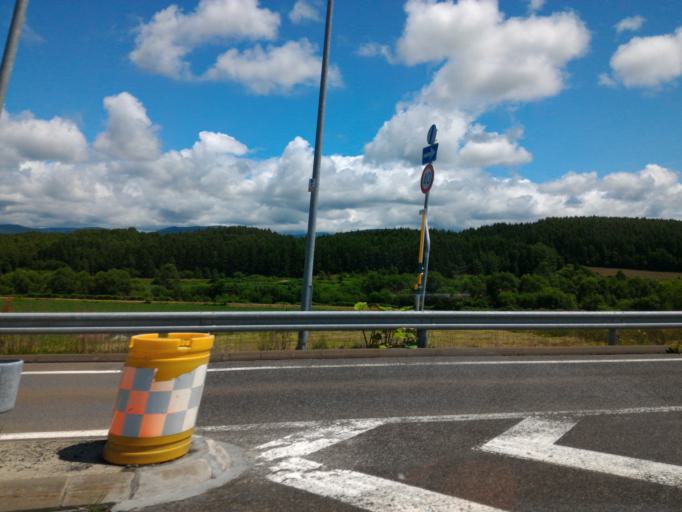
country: JP
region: Hokkaido
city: Nayoro
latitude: 44.4158
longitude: 142.4025
